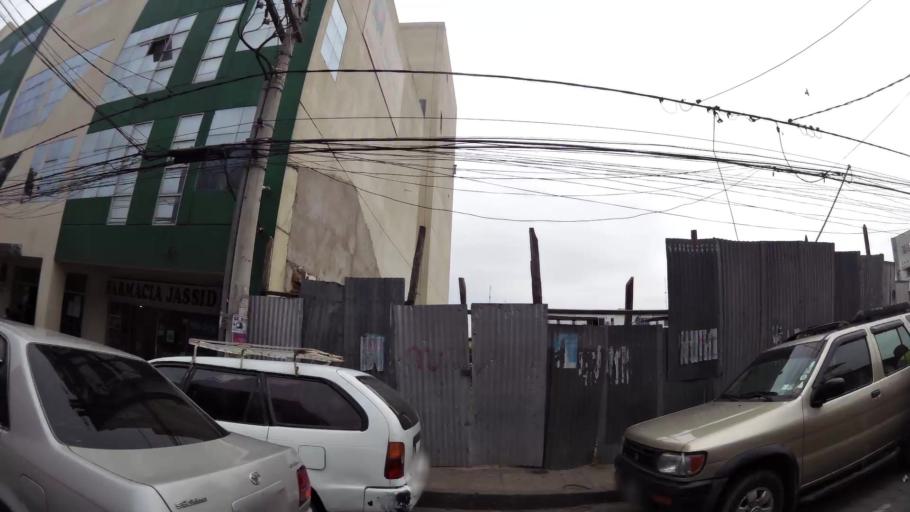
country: BO
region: Santa Cruz
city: Santa Cruz de la Sierra
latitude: -17.7825
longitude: -63.1872
